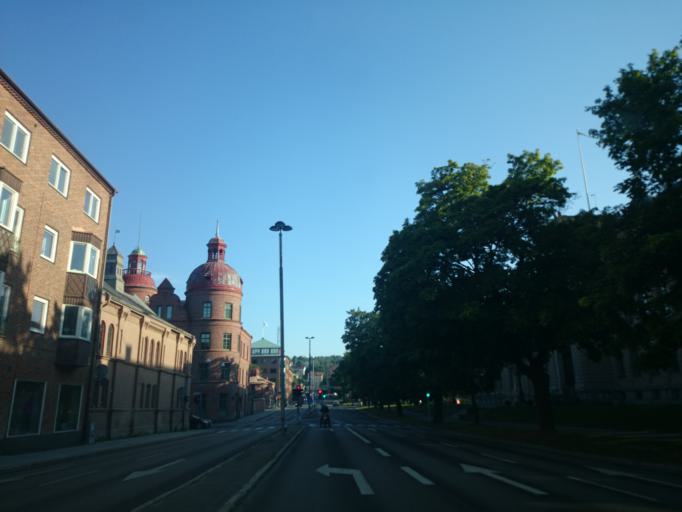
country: SE
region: Vaesternorrland
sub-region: Sundsvalls Kommun
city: Sundsvall
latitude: 62.3901
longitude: 17.3007
